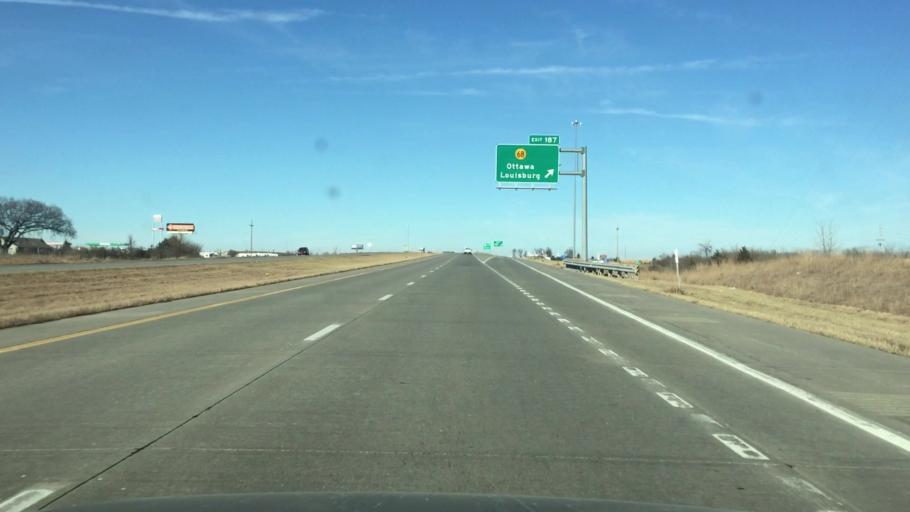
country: US
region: Kansas
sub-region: Franklin County
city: Ottawa
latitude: 38.6181
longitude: -95.2322
